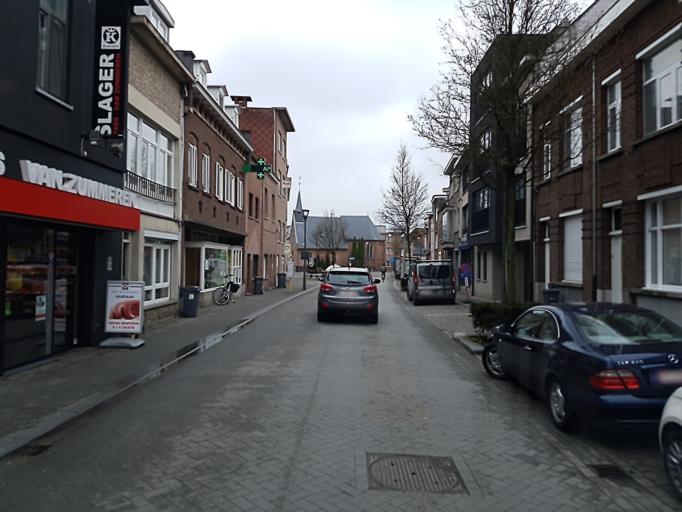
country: BE
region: Flanders
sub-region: Provincie Antwerpen
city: Turnhout
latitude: 51.3279
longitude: 4.9496
